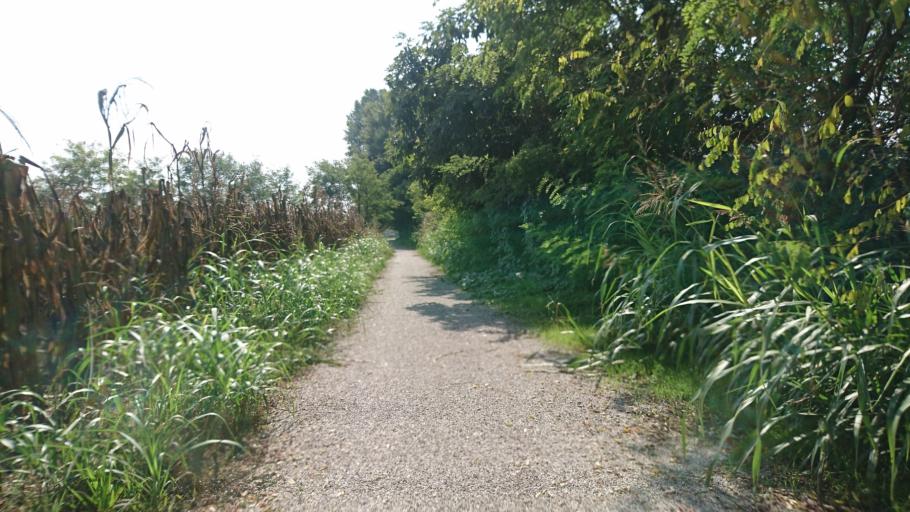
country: IT
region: Veneto
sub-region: Provincia di Padova
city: Piazzola sul Brenta
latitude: 45.5466
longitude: 11.8051
